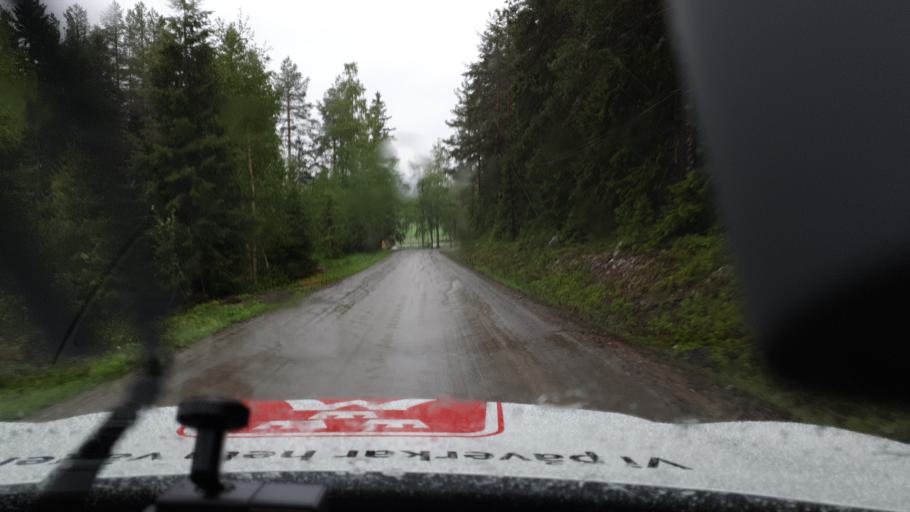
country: SE
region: Vaesterbotten
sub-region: Umea Kommun
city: Roback
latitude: 64.0077
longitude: 20.0710
